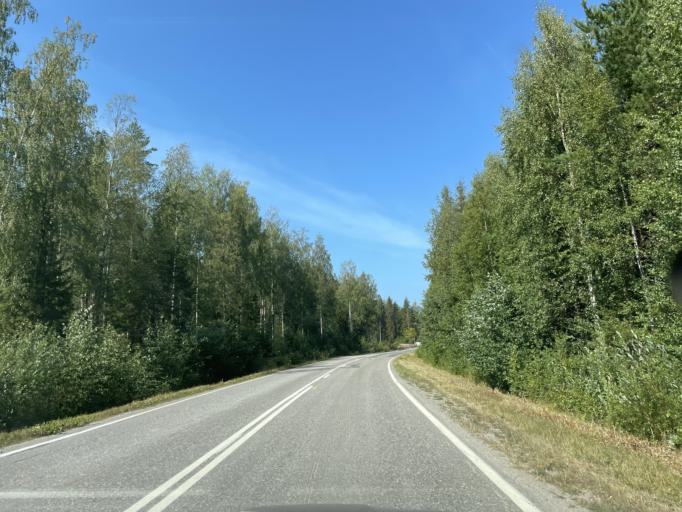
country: FI
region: Central Finland
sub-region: Saarijaervi-Viitasaari
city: Pihtipudas
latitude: 63.3671
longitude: 25.6295
